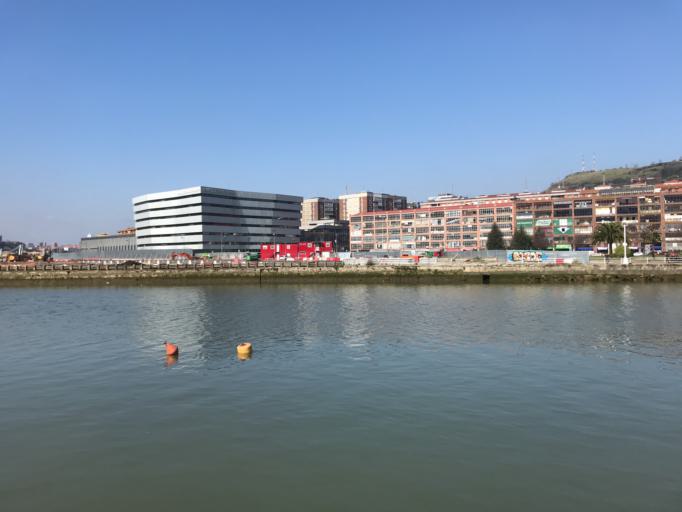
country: ES
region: Basque Country
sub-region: Bizkaia
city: Bilbao
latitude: 43.2661
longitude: -2.9495
